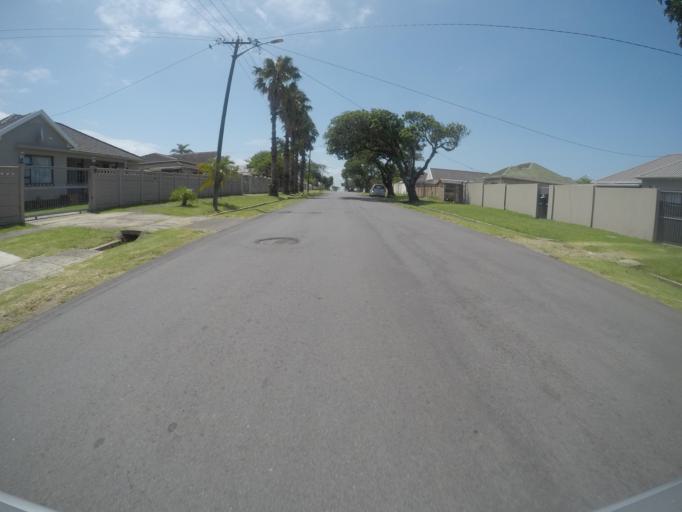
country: ZA
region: Eastern Cape
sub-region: Buffalo City Metropolitan Municipality
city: East London
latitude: -32.9743
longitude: 27.8811
